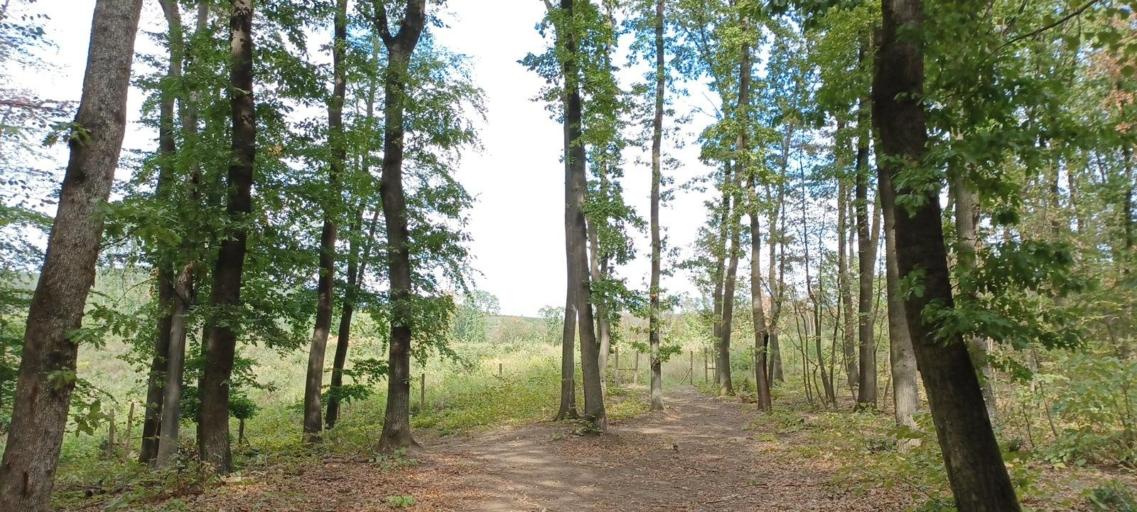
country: HU
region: Tolna
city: Szentgalpuszta
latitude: 46.3380
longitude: 18.6247
